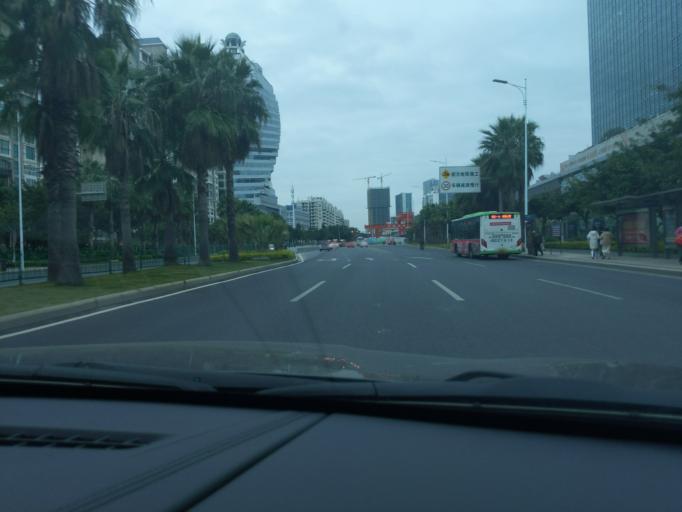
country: CN
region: Fujian
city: Liuwudian
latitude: 24.4841
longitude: 118.1777
